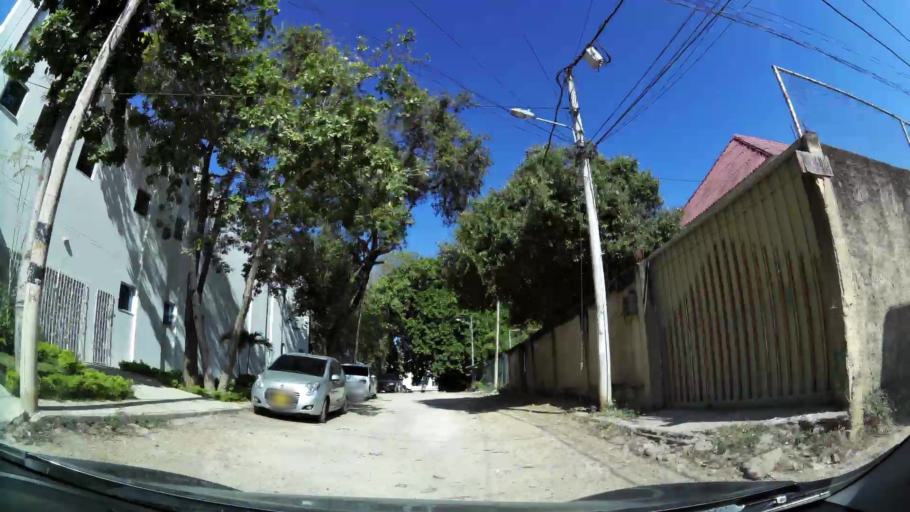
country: CO
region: Bolivar
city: Cartagena
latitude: 10.3937
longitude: -75.4753
